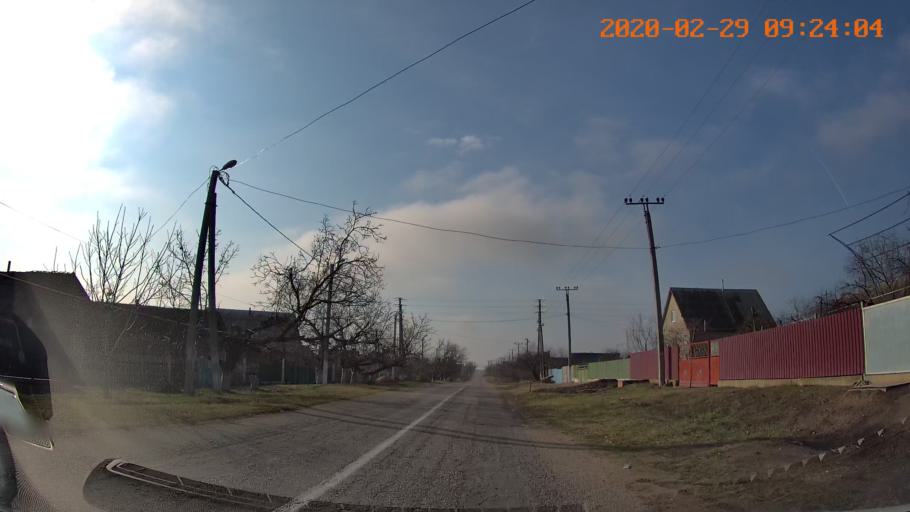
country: MD
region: Telenesti
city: Pervomaisc
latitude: 46.7197
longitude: 29.9596
